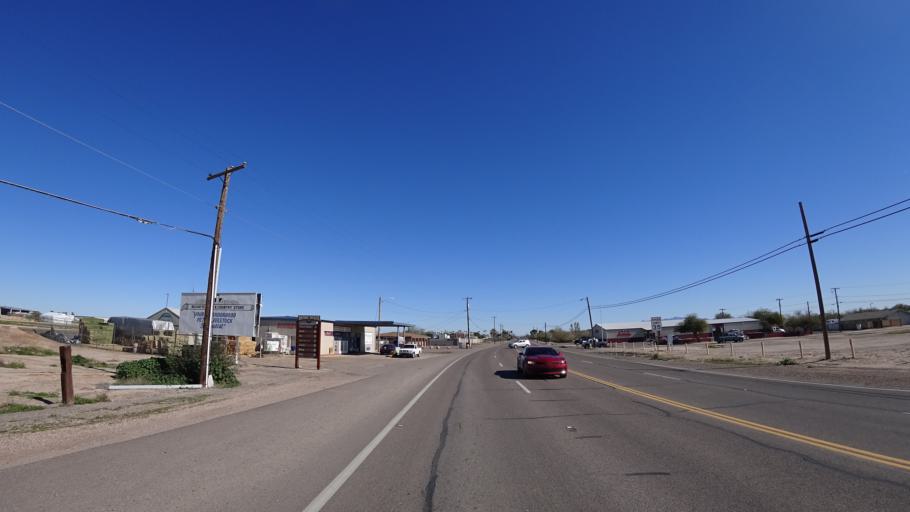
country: US
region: Arizona
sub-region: Maricopa County
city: Buckeye
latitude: 33.3776
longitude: -112.5692
